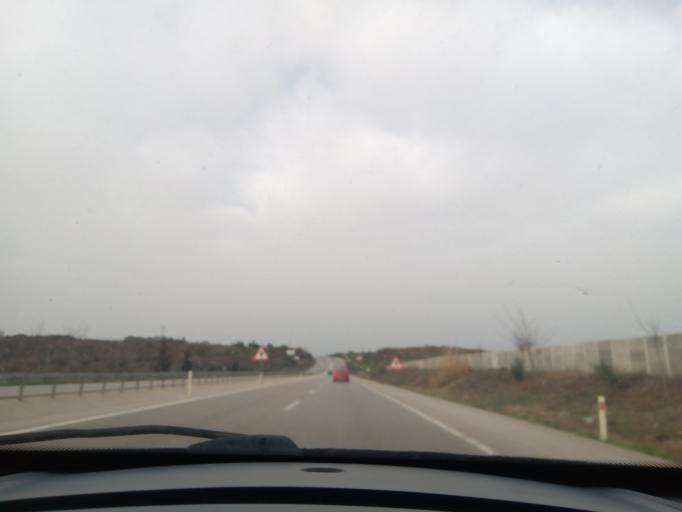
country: TR
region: Bursa
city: Mahmudiye
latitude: 40.2171
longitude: 28.6482
